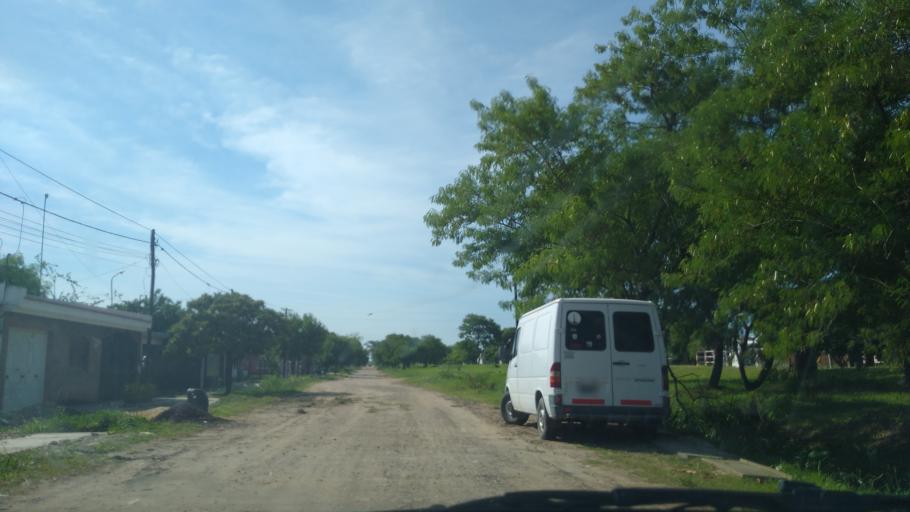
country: AR
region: Chaco
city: Barranqueras
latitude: -27.4907
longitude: -58.9509
